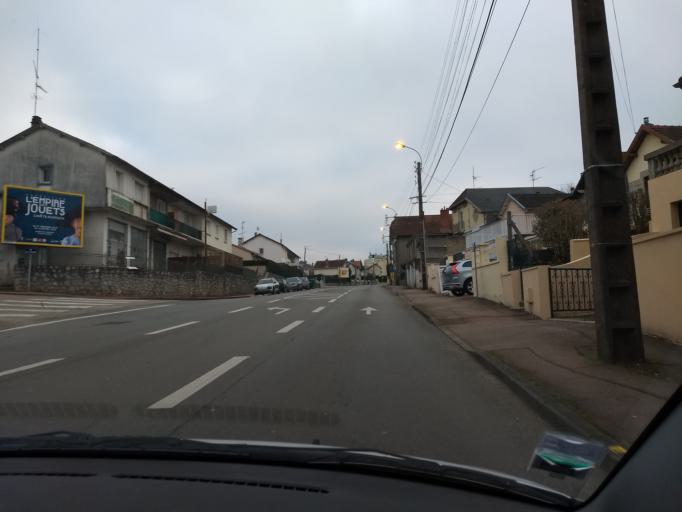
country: FR
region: Limousin
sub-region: Departement de la Haute-Vienne
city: Isle
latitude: 45.8223
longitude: 1.2172
